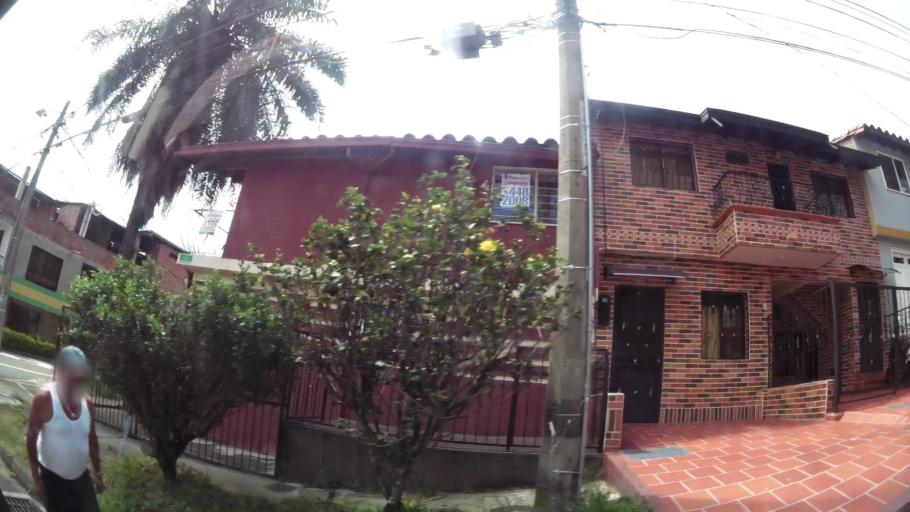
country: CO
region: Antioquia
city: Bello
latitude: 6.3127
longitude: -75.5608
